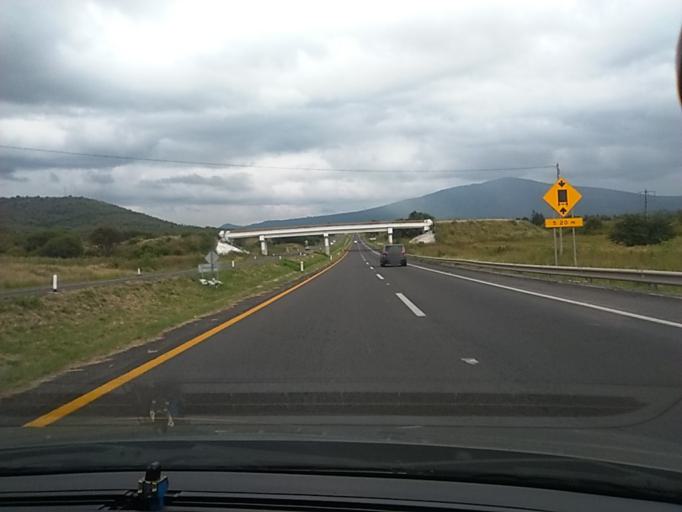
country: MX
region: Jalisco
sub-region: Zapotlanejo
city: La Mezquitera
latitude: 20.5788
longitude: -103.0916
